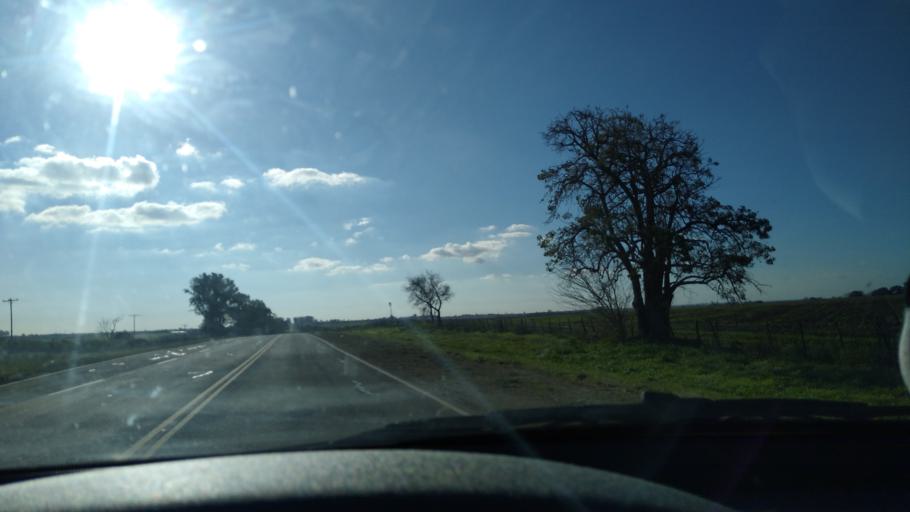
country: AR
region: Entre Rios
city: Diamante
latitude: -32.1226
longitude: -60.5659
